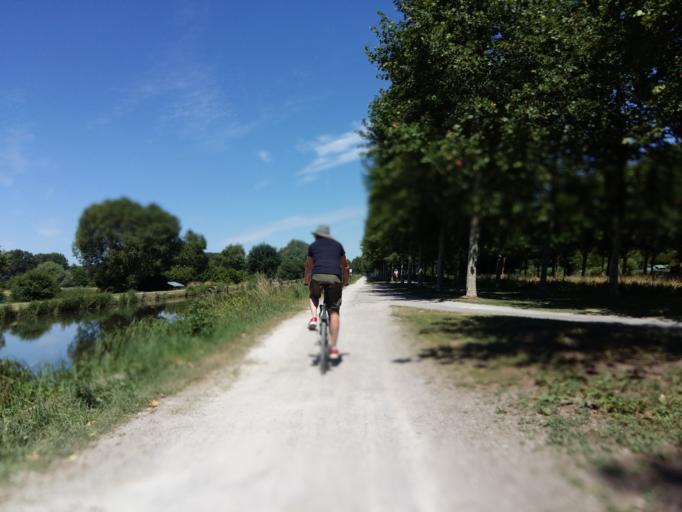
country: FR
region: Picardie
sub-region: Departement de la Somme
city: Amiens
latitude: 49.9100
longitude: 2.2803
